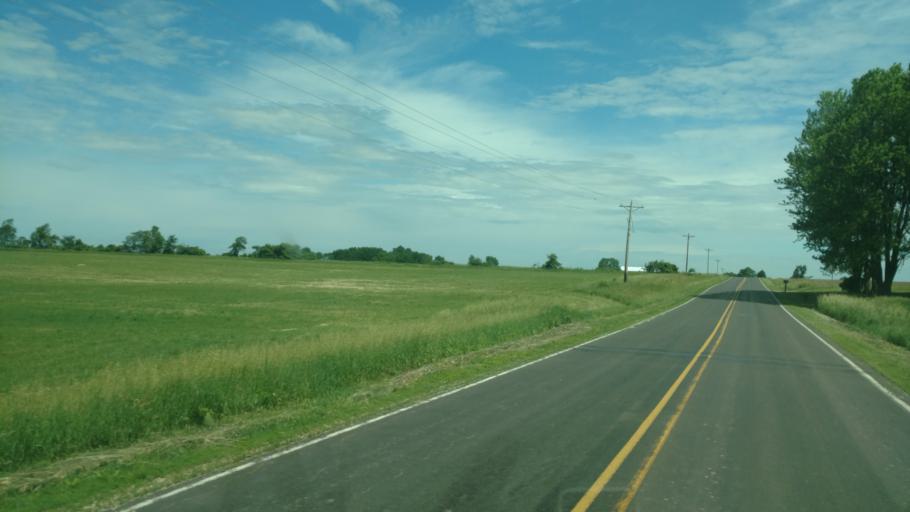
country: US
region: Wisconsin
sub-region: Vernon County
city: Hillsboro
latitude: 43.7073
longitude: -90.4527
